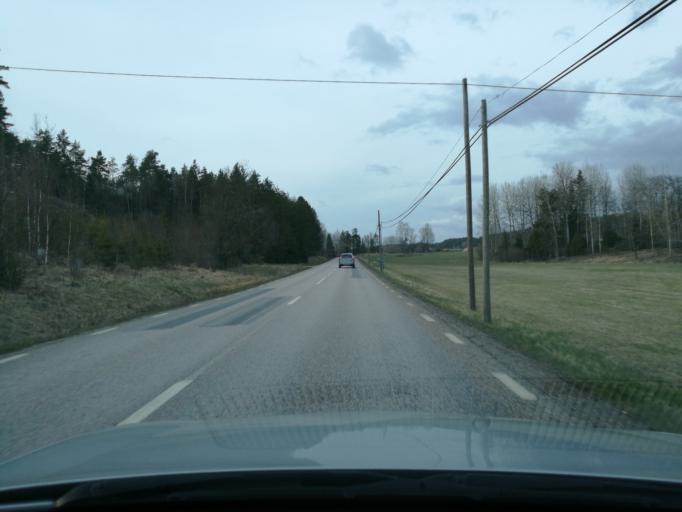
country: SE
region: Soedermanland
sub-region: Gnesta Kommun
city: Gnesta
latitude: 58.9589
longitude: 17.3509
